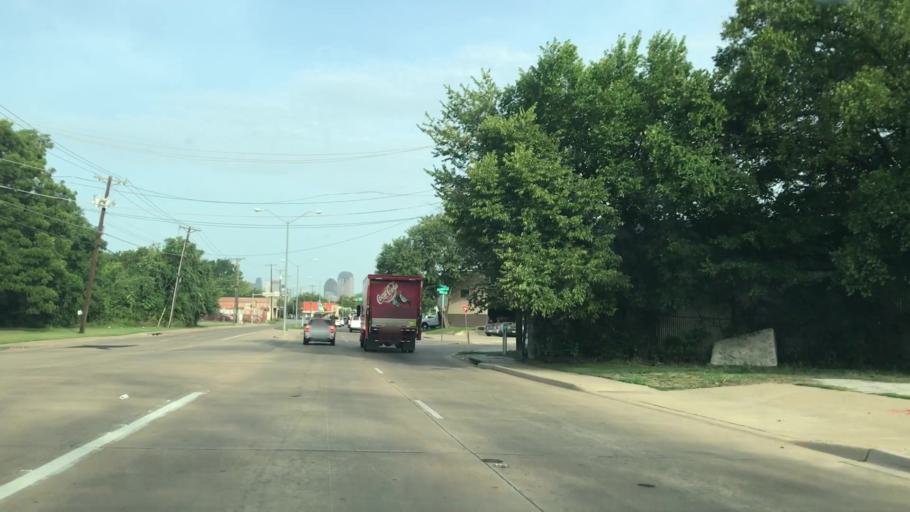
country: US
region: Texas
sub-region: Dallas County
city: Dallas
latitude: 32.7838
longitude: -96.7560
